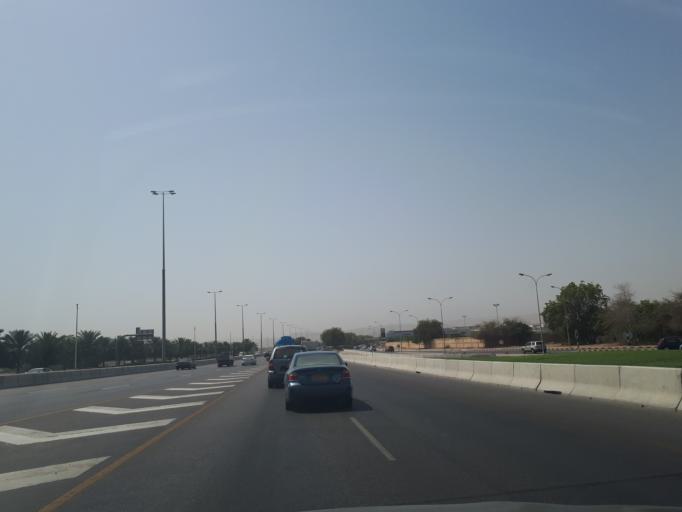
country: OM
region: Muhafazat Masqat
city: As Sib al Jadidah
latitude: 23.6090
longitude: 58.2469
